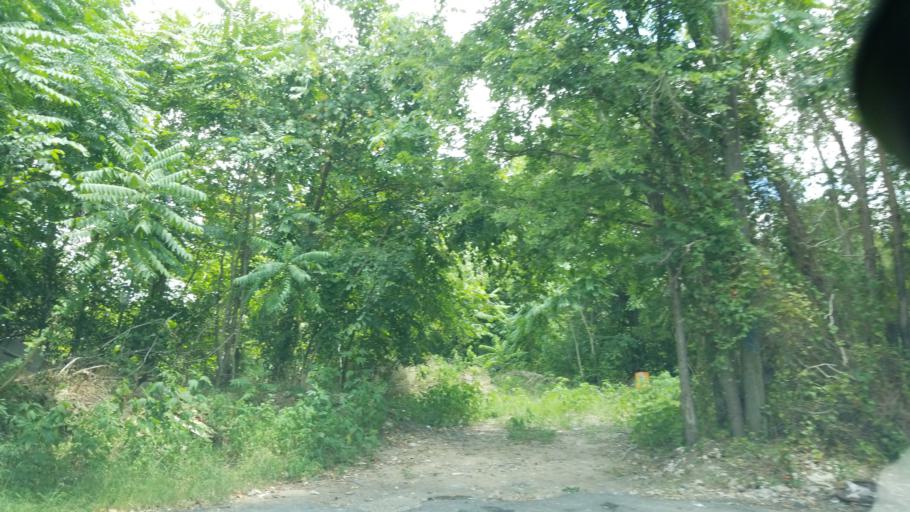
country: US
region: Texas
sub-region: Dallas County
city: Dallas
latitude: 32.7233
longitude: -96.7562
